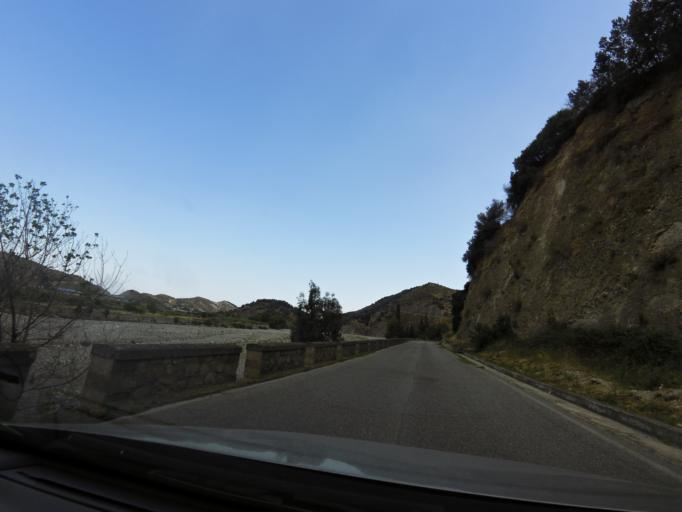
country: IT
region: Calabria
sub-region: Provincia di Reggio Calabria
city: Stilo
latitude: 38.4633
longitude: 16.4942
